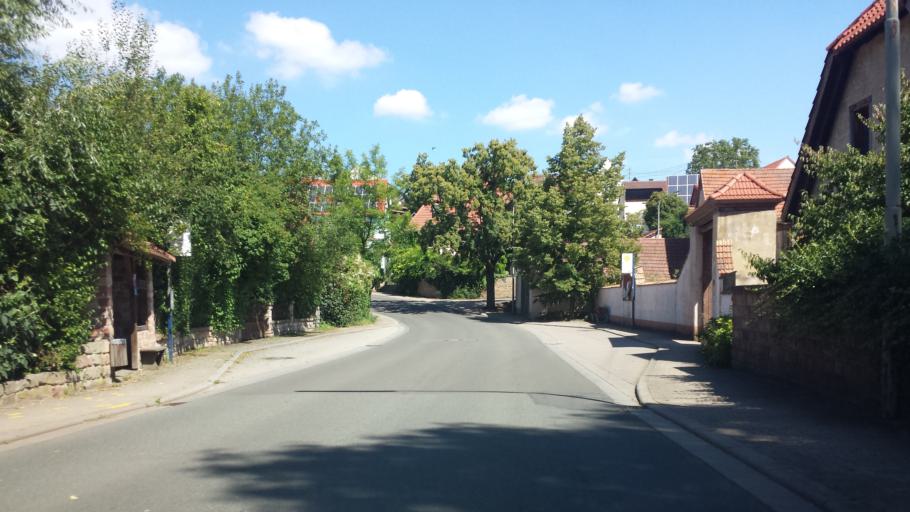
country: DE
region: Rheinland-Pfalz
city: Weitersweiler
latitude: 49.6141
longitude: 7.9977
